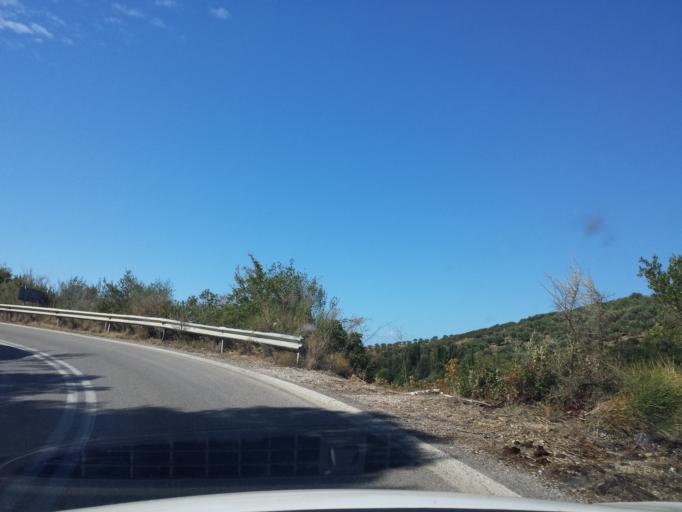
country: GR
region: Peloponnese
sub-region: Nomos Messinias
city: Pylos
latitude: 36.9423
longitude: 21.7432
